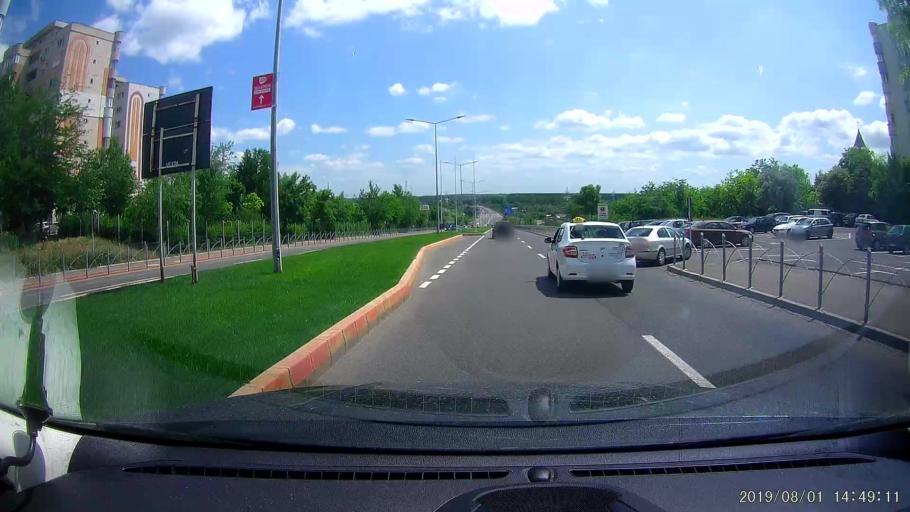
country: RO
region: Galati
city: Galati
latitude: 45.4084
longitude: 28.0151
